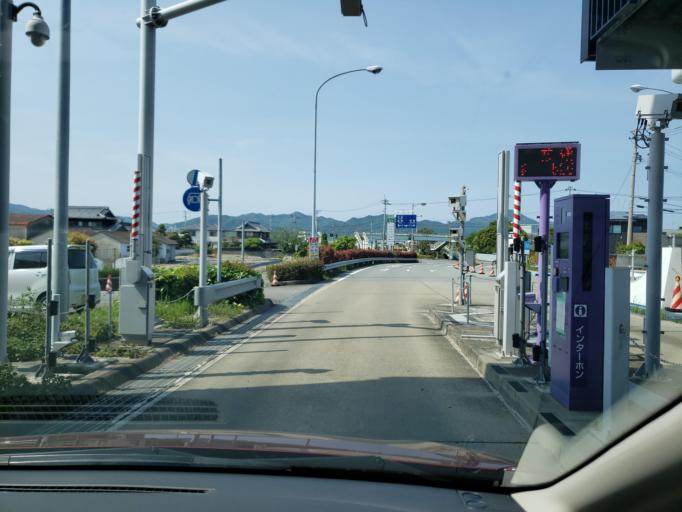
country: JP
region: Tokushima
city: Ishii
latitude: 34.1191
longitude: 134.4795
